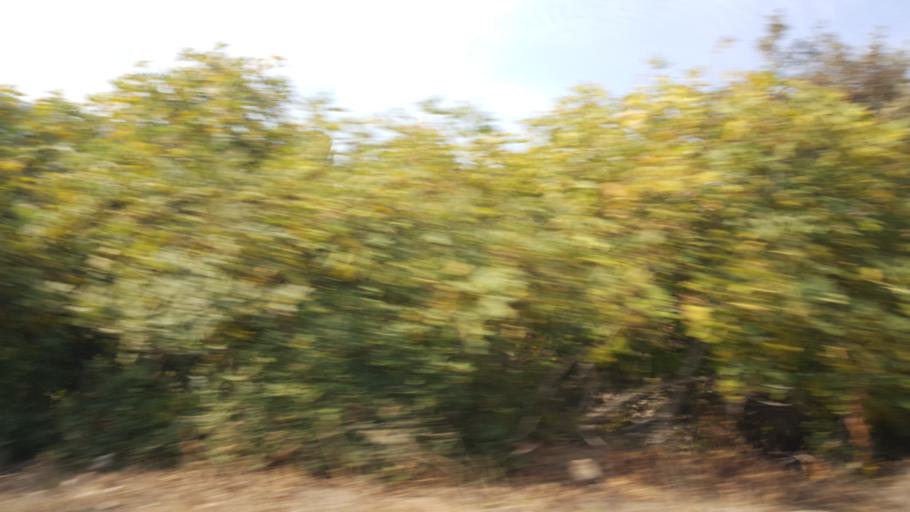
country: TR
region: Eskisehir
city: Mihaliccik
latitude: 39.9802
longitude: 31.3752
